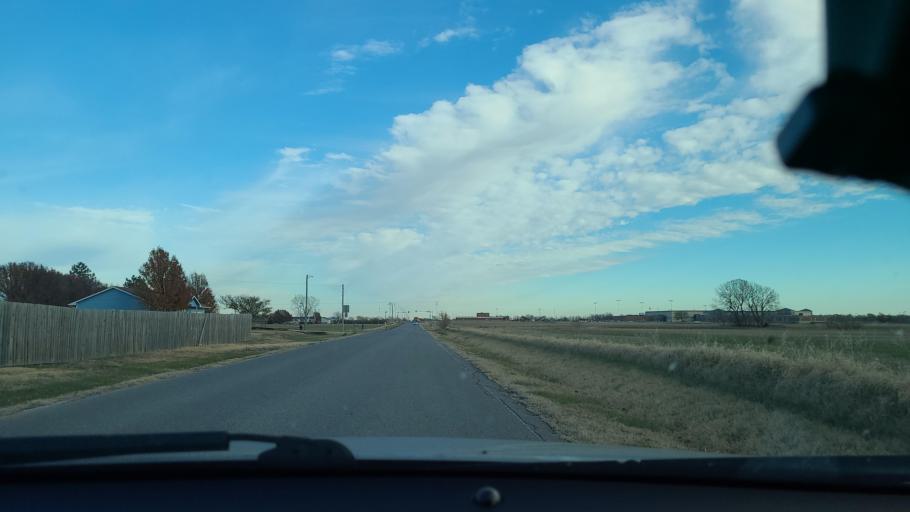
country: US
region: Kansas
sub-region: Sedgwick County
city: Goddard
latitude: 37.6496
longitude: -97.5762
